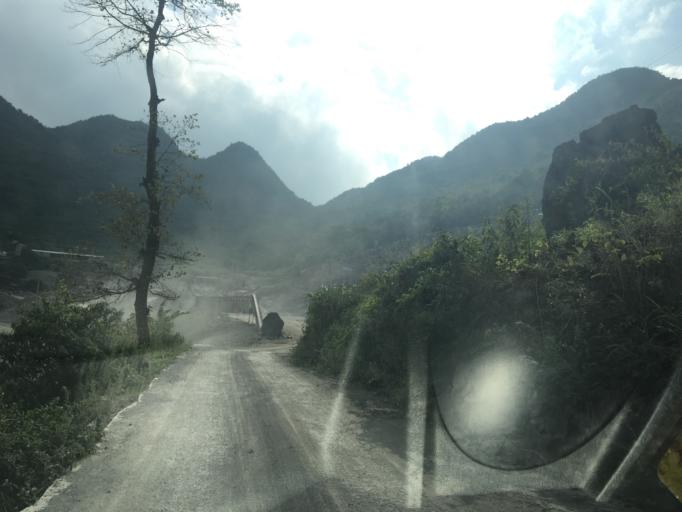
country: CN
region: Guangxi Zhuangzu Zizhiqu
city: Xinzhou
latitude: 25.0671
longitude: 105.7227
